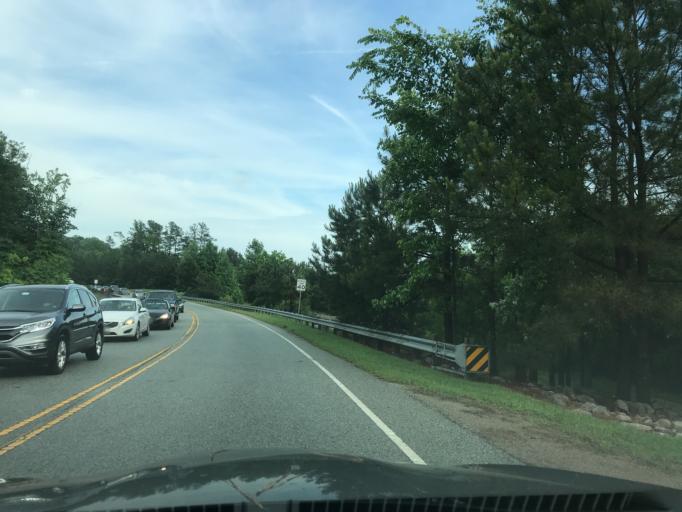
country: US
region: North Carolina
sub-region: Wake County
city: Morrisville
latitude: 35.8571
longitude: -78.8819
